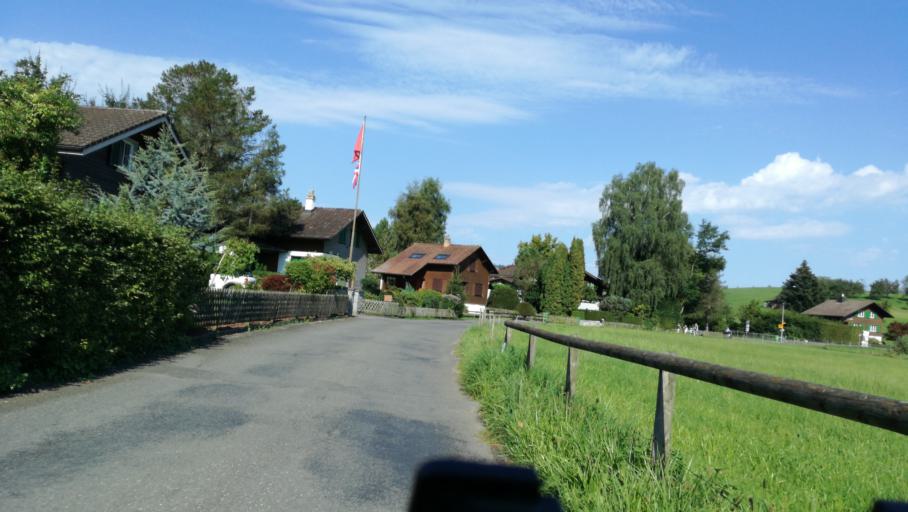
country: CH
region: Zug
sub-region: Zug
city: Unterageri
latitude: 47.1223
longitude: 8.5918
